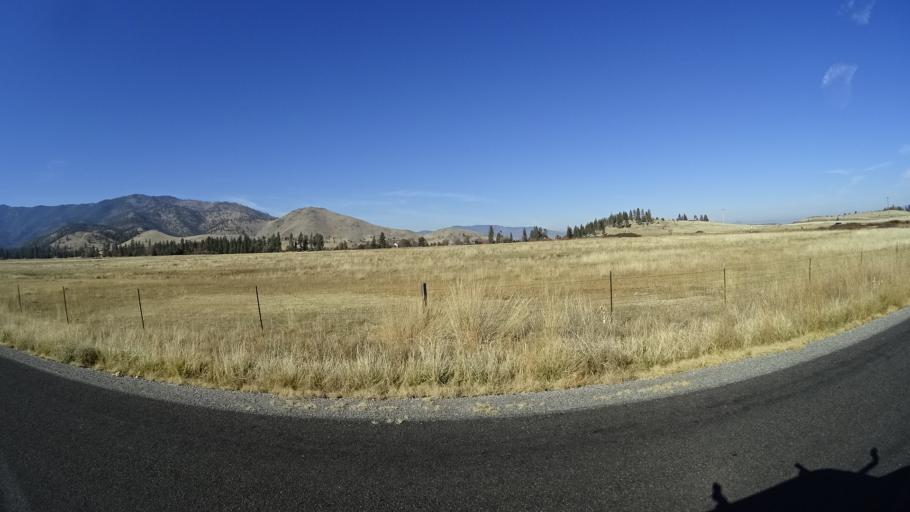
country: US
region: California
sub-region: Siskiyou County
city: Weed
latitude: 41.4432
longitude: -122.4437
